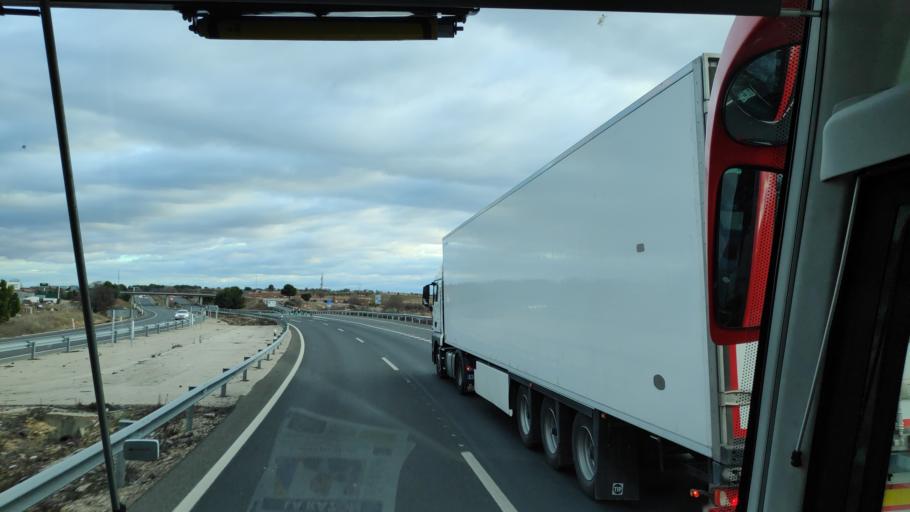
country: ES
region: Madrid
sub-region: Provincia de Madrid
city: Villarejo de Salvanes
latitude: 40.1746
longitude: -3.2952
